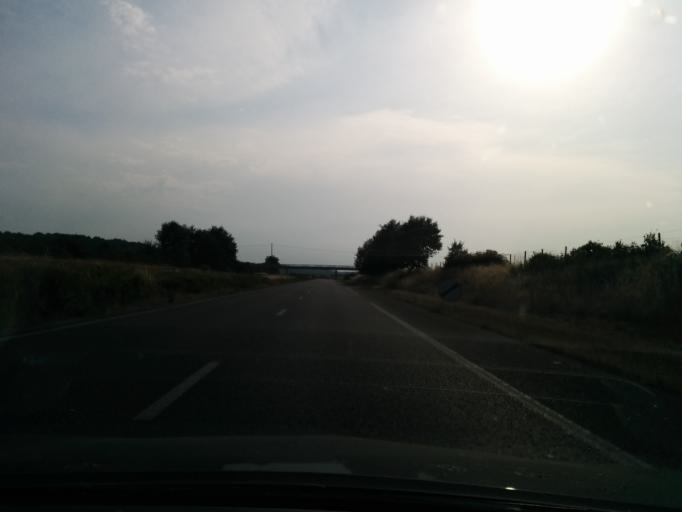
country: FR
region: Midi-Pyrenees
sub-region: Departement de la Haute-Garonne
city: Buzet-sur-Tarn
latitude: 43.7532
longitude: 1.6536
